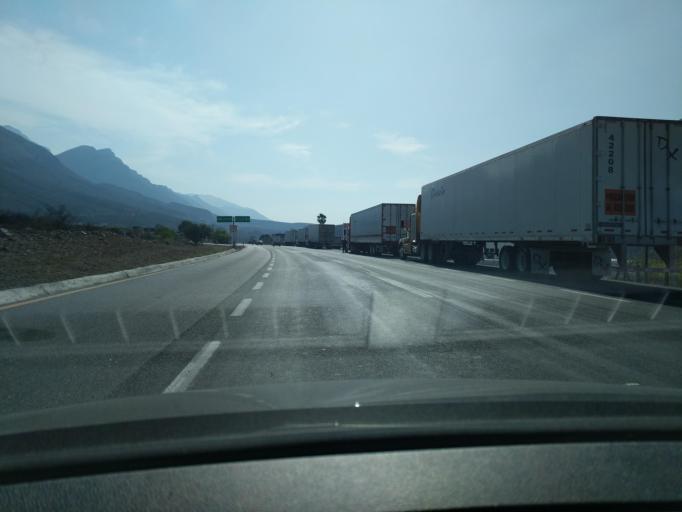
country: MX
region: Nuevo Leon
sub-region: Garcia
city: Las Torres de Guadalupe
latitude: 25.6608
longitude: -100.7138
